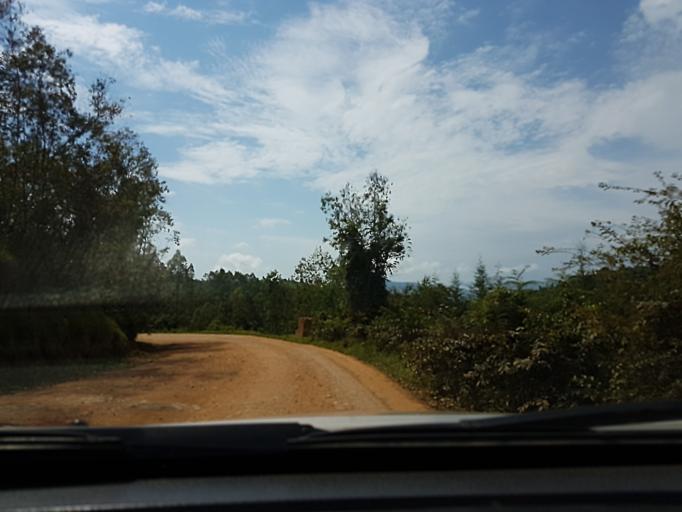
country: CD
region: South Kivu
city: Bukavu
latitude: -2.6301
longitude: 28.8748
